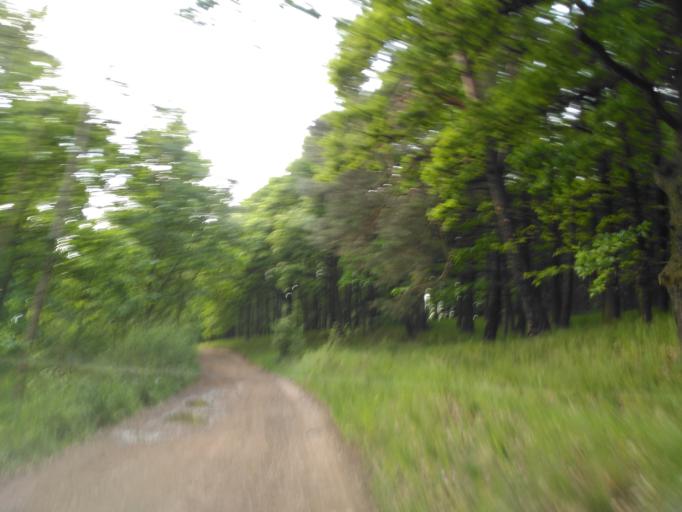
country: CZ
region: Plzensky
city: Zbiroh
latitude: 49.8584
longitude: 13.7420
